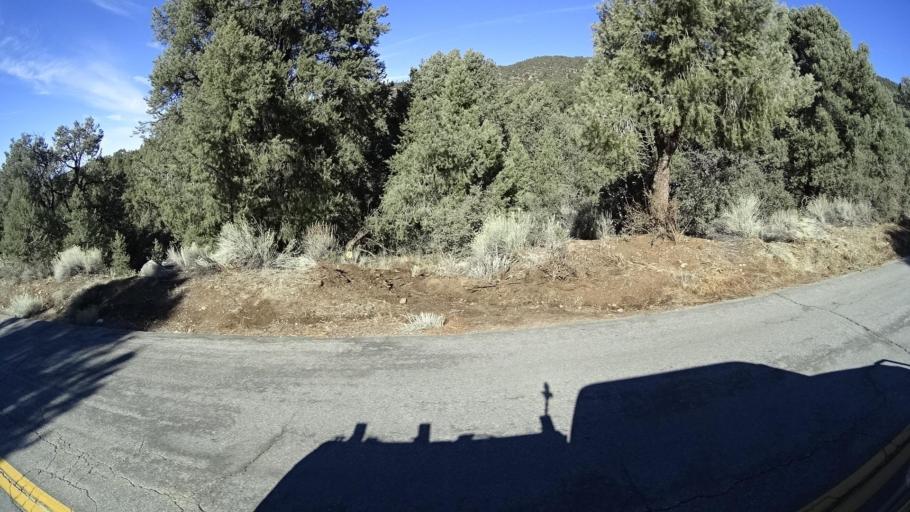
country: US
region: California
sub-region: Kern County
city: Pine Mountain Club
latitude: 34.8612
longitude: -119.2175
